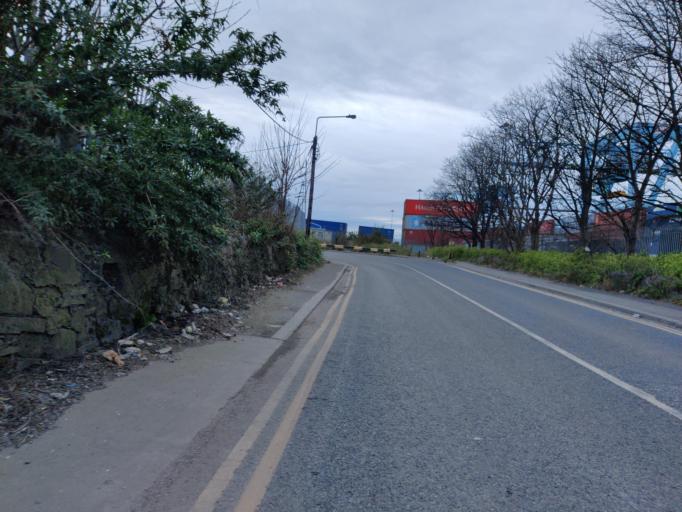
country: IE
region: Leinster
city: Sandymount
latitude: 53.3418
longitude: -6.2071
